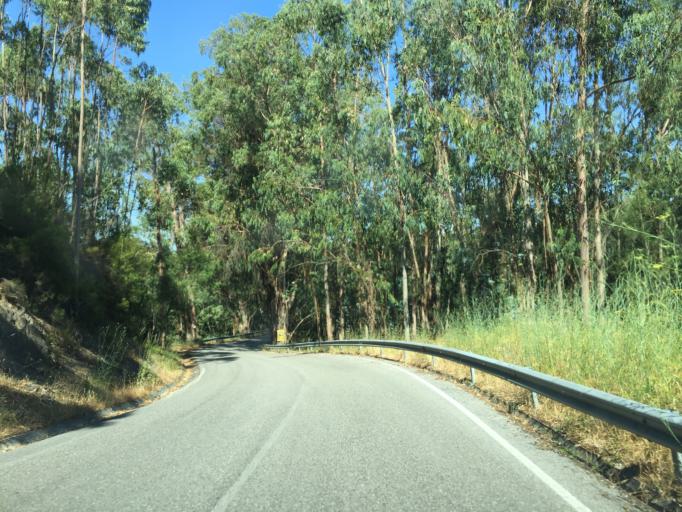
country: PT
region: Santarem
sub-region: Tomar
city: Tomar
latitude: 39.6052
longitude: -8.3447
